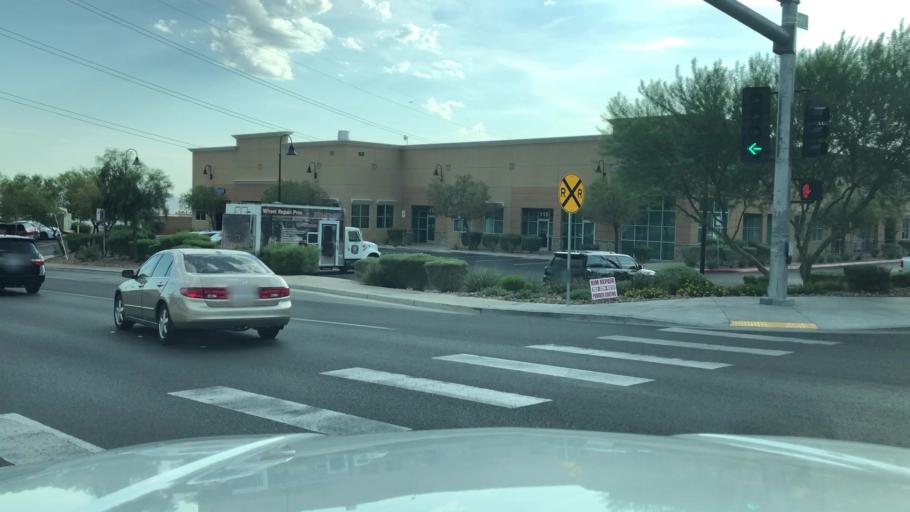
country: US
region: Nevada
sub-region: Clark County
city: Henderson
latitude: 36.0342
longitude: -115.0294
